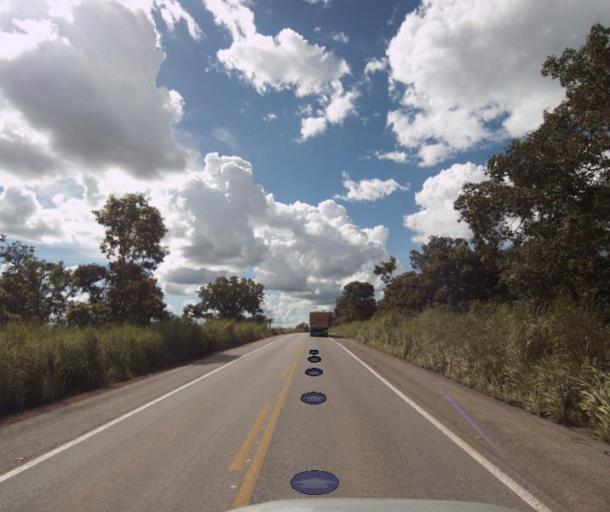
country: BR
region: Goias
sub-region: Porangatu
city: Porangatu
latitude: -13.2386
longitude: -49.1427
